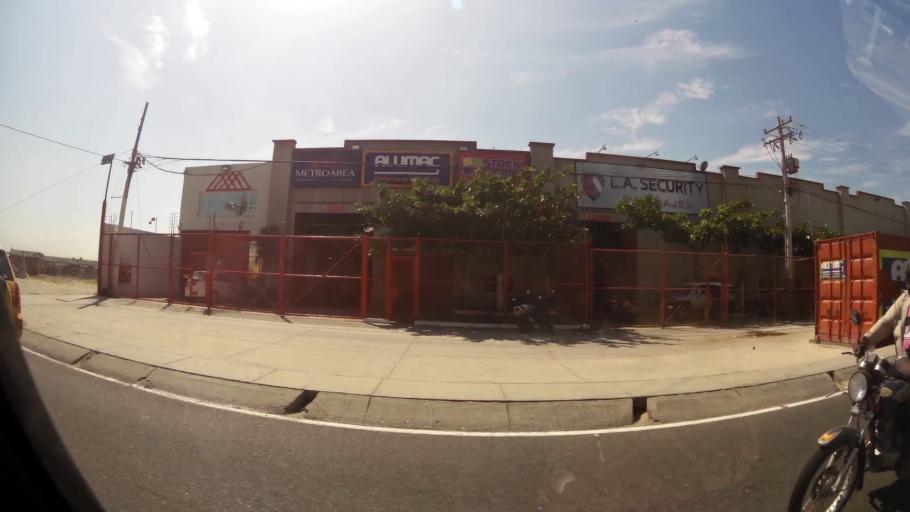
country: CO
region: Atlantico
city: Barranquilla
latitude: 10.9603
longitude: -74.8375
